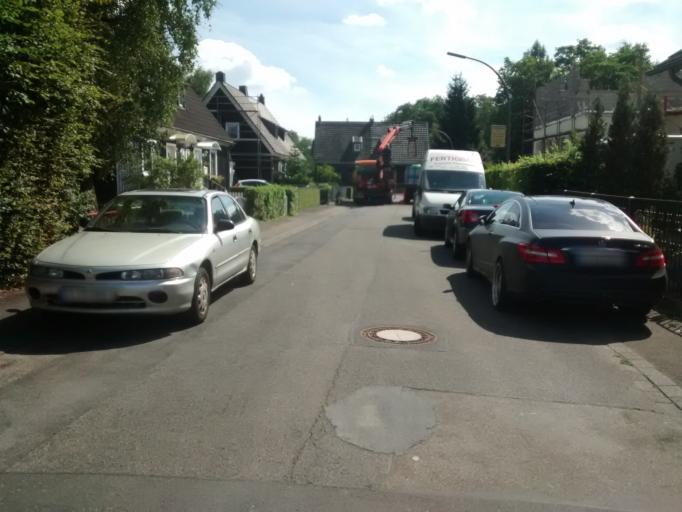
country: DE
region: North Rhine-Westphalia
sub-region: Regierungsbezirk Koln
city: Buchheim
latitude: 50.9886
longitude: 7.0415
